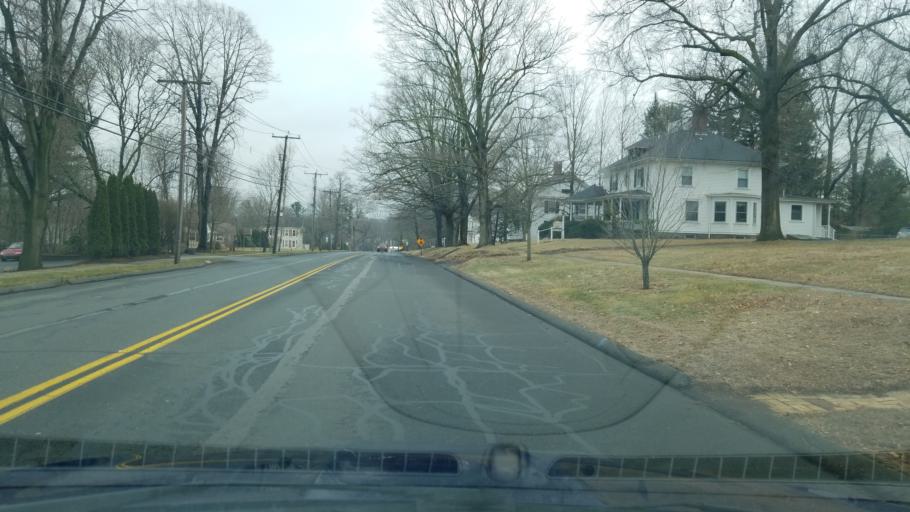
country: US
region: Connecticut
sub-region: Hartford County
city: Wethersfield
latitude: 41.6863
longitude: -72.6720
